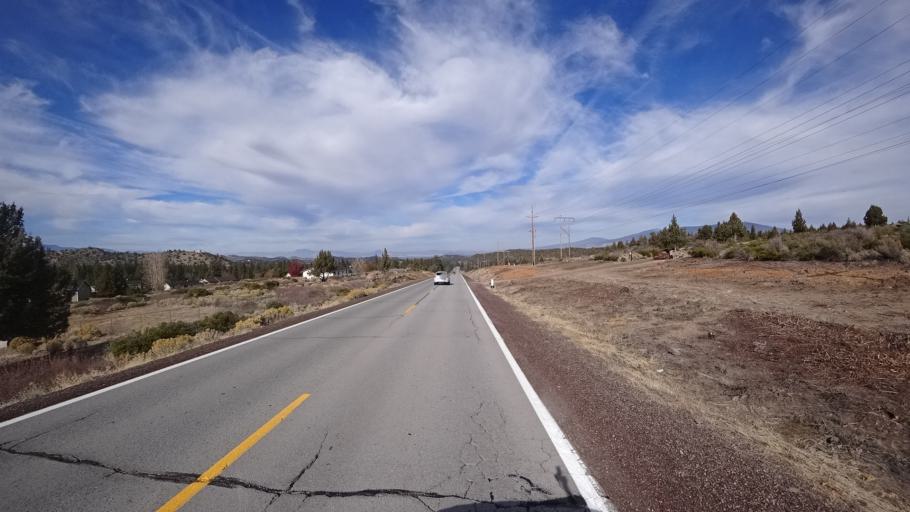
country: US
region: California
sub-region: Siskiyou County
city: Weed
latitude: 41.4980
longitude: -122.3629
